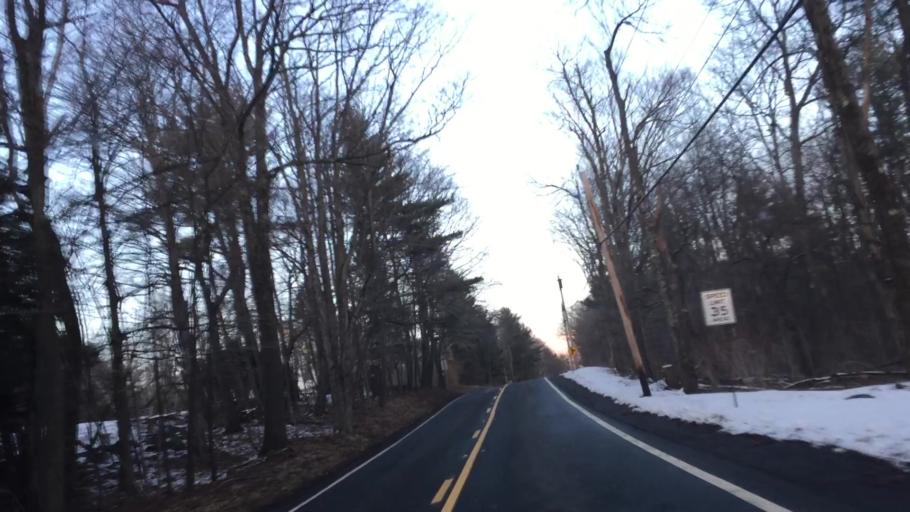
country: US
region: Massachusetts
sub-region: Berkshire County
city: Otis
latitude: 42.1721
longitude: -72.9993
